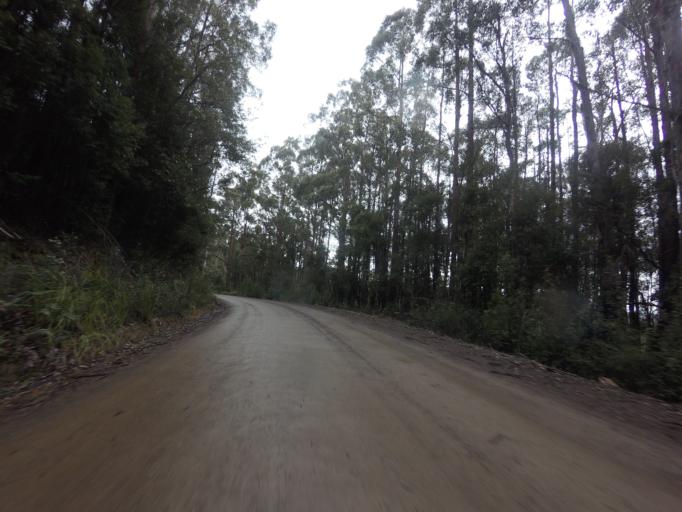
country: AU
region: Tasmania
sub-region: Huon Valley
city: Geeveston
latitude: -43.4831
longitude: 146.8924
